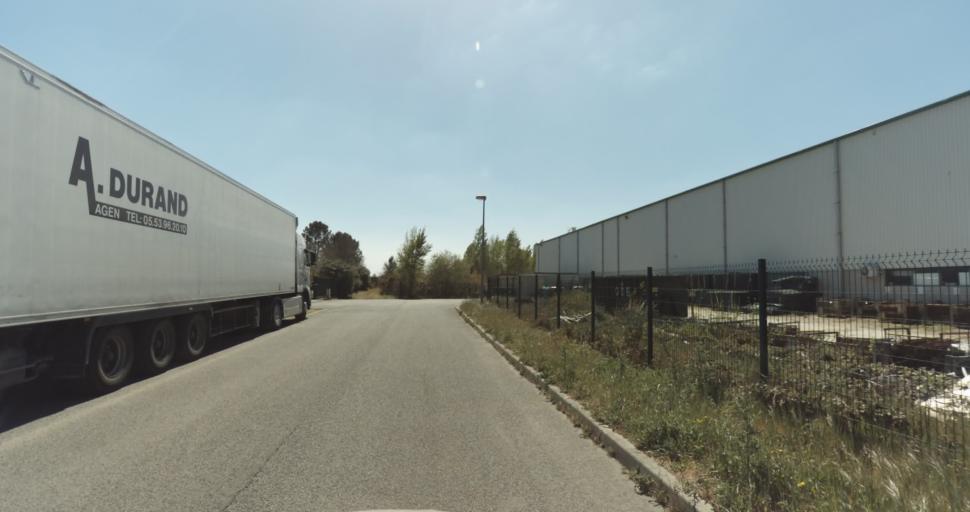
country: FR
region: Aquitaine
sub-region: Departement de la Gironde
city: Martignas-sur-Jalle
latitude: 44.8075
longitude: -0.7451
